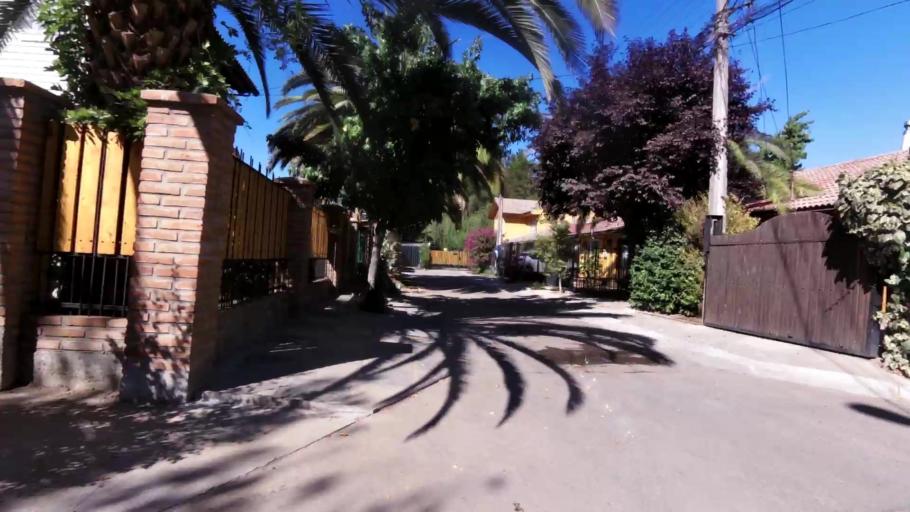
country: CL
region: O'Higgins
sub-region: Provincia de Cachapoal
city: Rancagua
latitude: -34.1830
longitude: -70.7087
